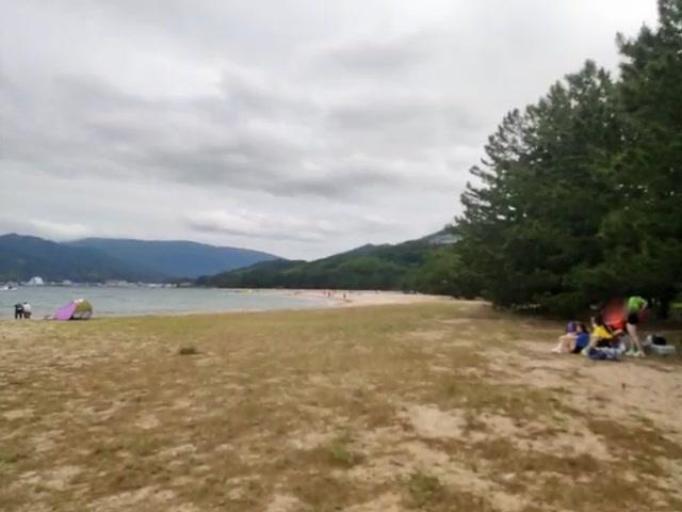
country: JP
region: Kyoto
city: Miyazu
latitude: 35.5609
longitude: 135.1878
